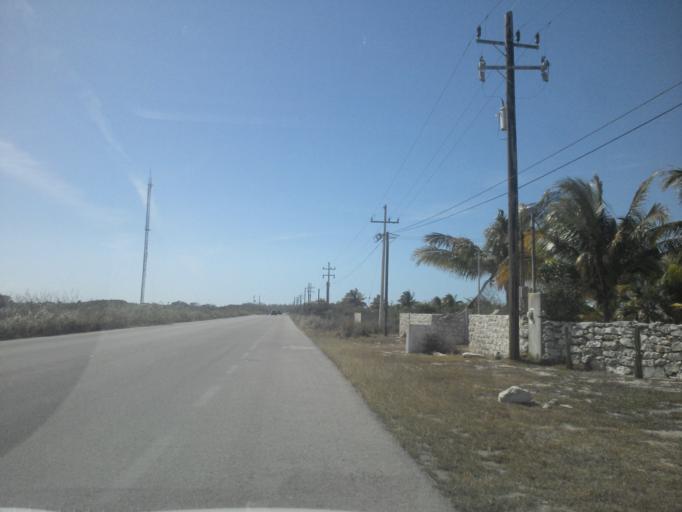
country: MX
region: Yucatan
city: Telchac Puerto
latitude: 21.3287
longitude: -89.3910
